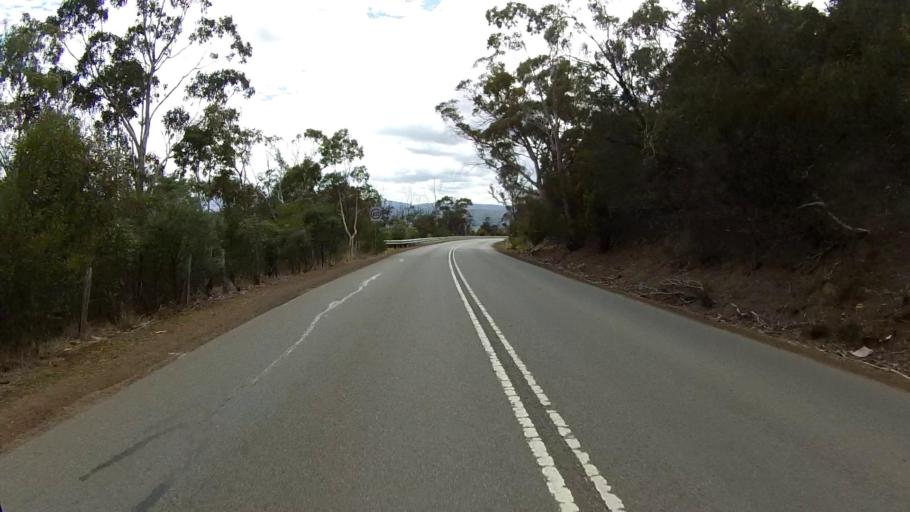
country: AU
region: Tasmania
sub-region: Clarence
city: Lindisfarne
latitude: -42.7799
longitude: 147.3663
